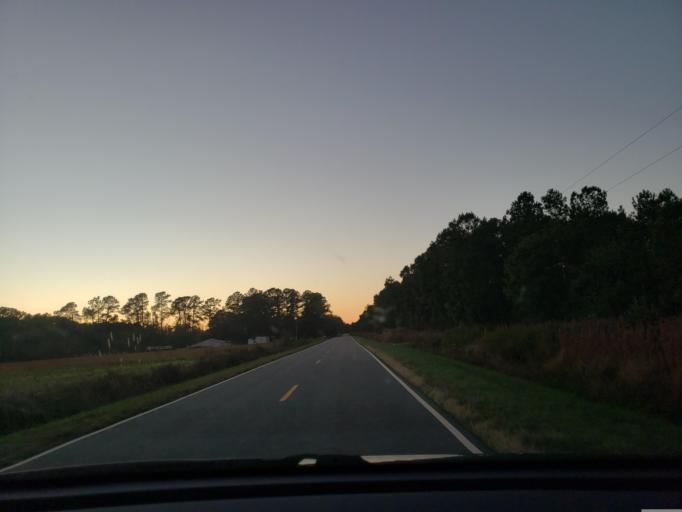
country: US
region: North Carolina
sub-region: Duplin County
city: Beulaville
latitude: 34.7641
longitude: -77.7200
